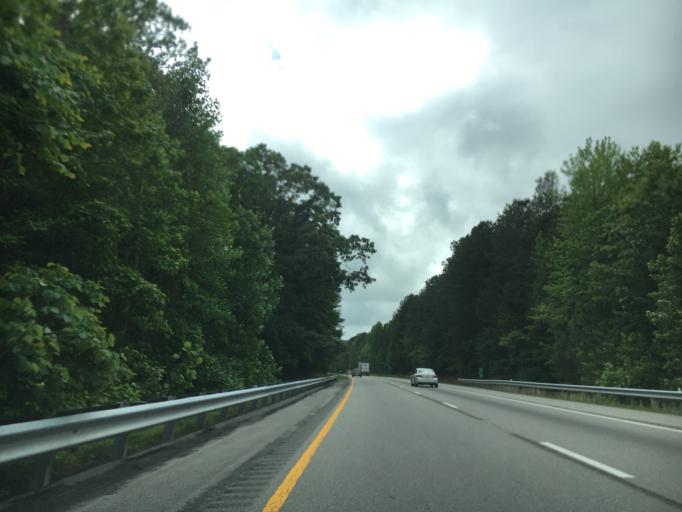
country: US
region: Virginia
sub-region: Mecklenburg County
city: South Hill
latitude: 36.7597
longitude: -78.0857
